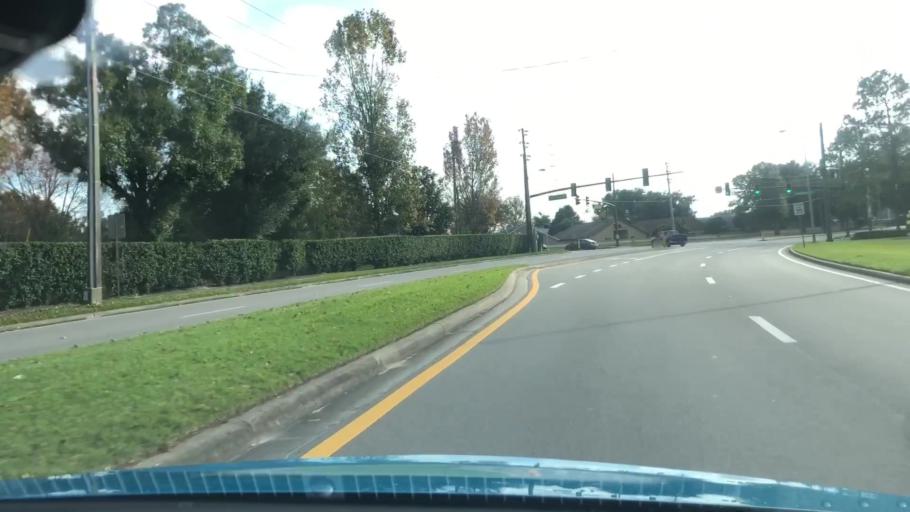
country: US
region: Florida
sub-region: Seminole County
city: Lake Mary
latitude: 28.7481
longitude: -81.3444
